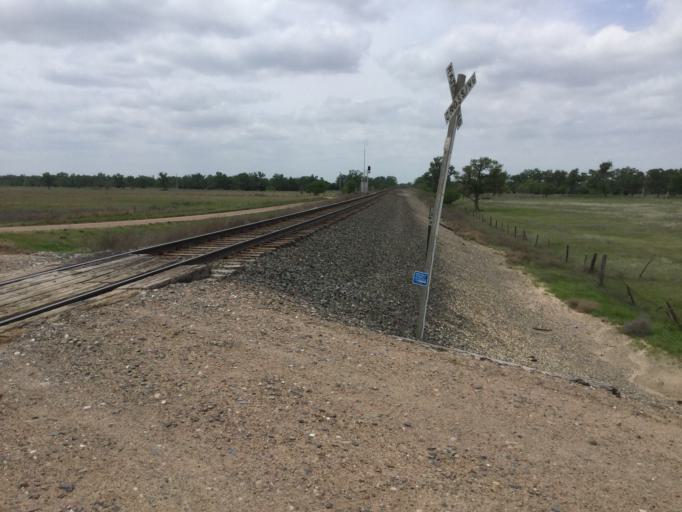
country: US
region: Kansas
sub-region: Edwards County
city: Kinsley
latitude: 37.9352
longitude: -99.3657
